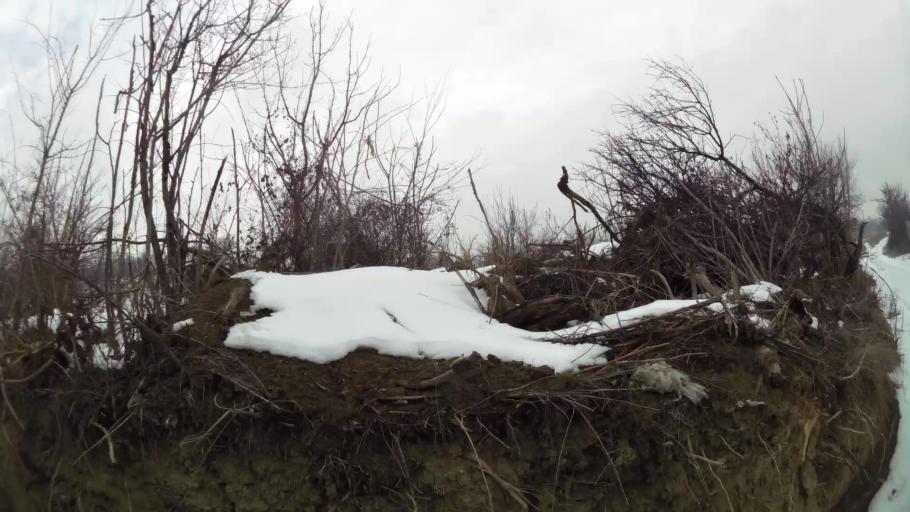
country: MK
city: Kondovo
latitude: 42.0349
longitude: 21.3380
